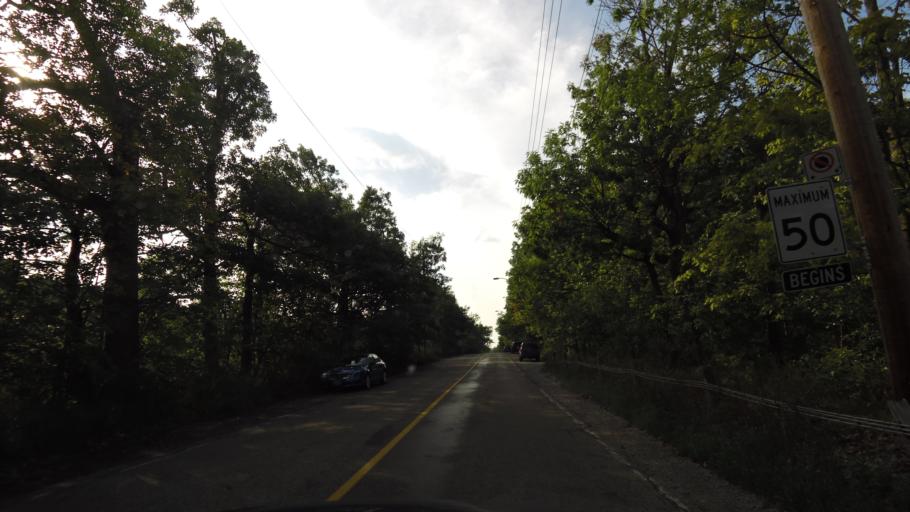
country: CA
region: Ontario
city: Burlington
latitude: 43.3484
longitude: -79.8619
